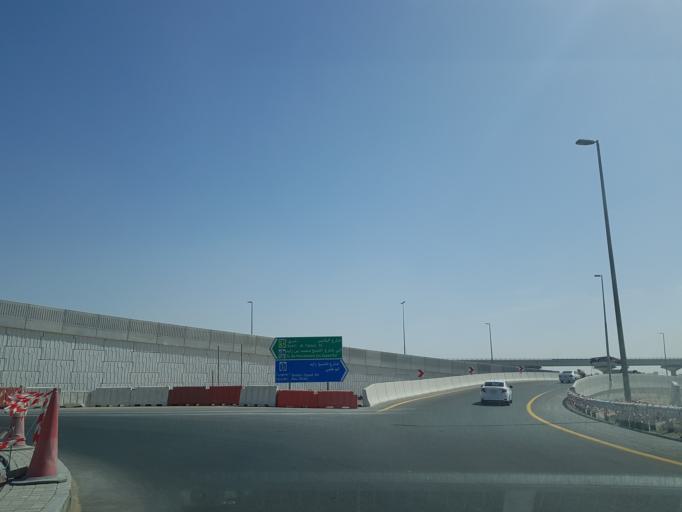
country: AE
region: Dubai
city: Dubai
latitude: 25.0121
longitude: 55.0955
